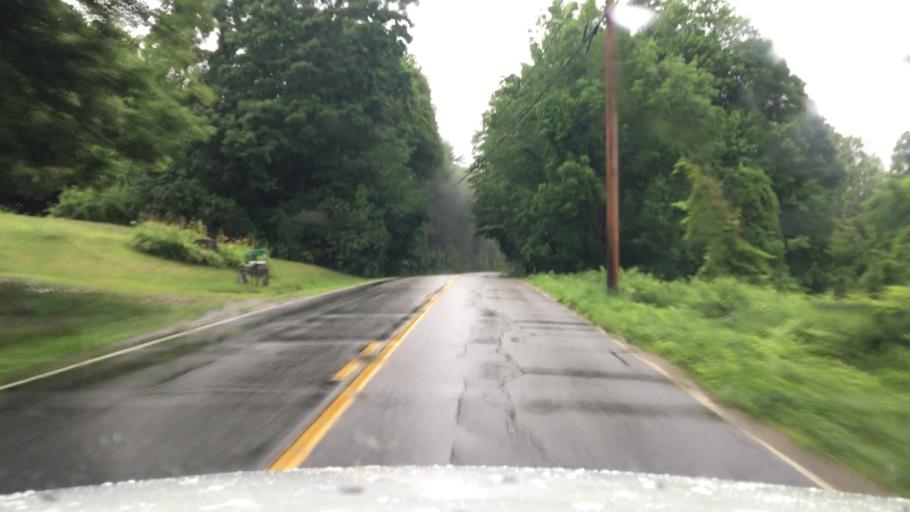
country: US
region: Maine
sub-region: Kennebec County
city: Winthrop
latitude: 44.2972
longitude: -69.9271
